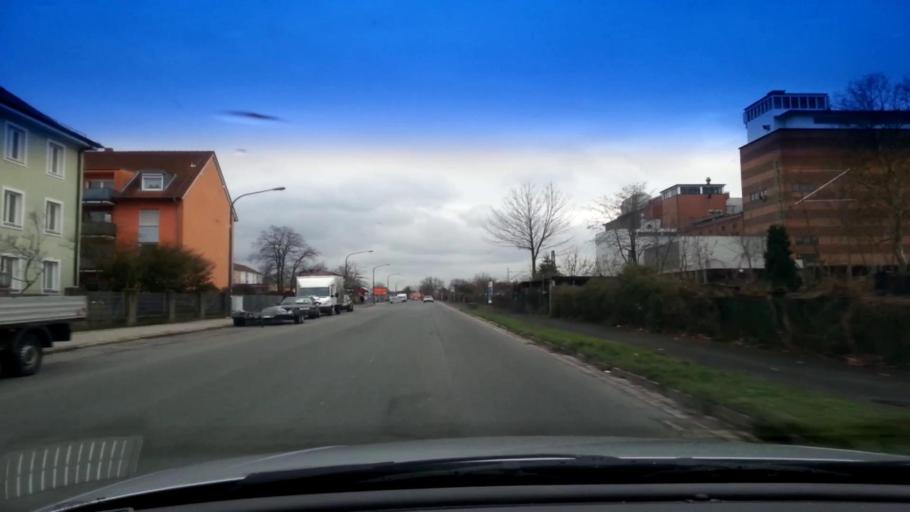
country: DE
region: Bavaria
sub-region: Upper Franconia
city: Bamberg
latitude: 49.8884
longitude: 10.9137
